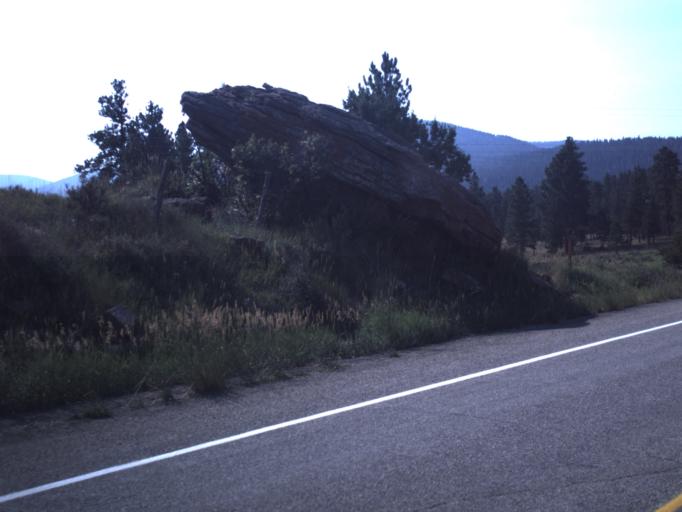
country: US
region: Utah
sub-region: Daggett County
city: Manila
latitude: 40.8859
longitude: -109.4553
